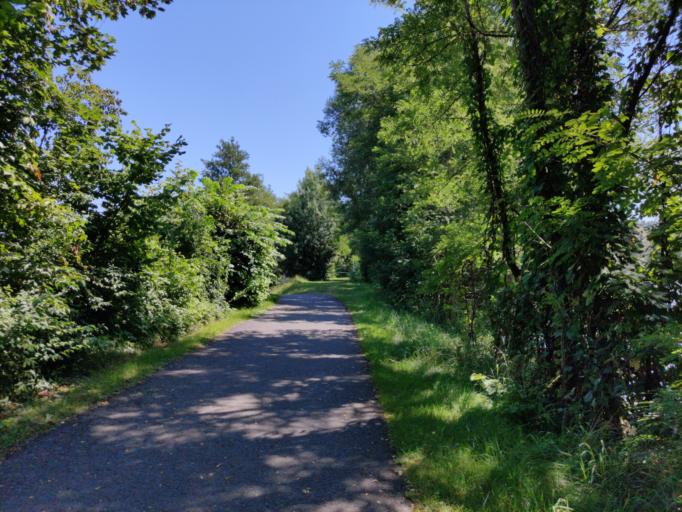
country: AT
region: Styria
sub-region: Politischer Bezirk Leibnitz
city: Ehrenhausen
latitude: 46.7290
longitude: 15.5858
